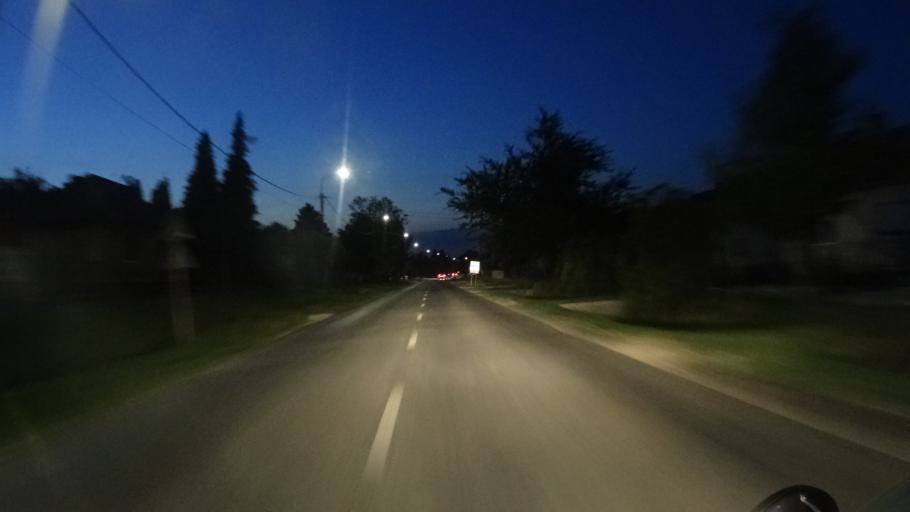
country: HU
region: Somogy
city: Balatonbereny
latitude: 46.6994
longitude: 17.3700
